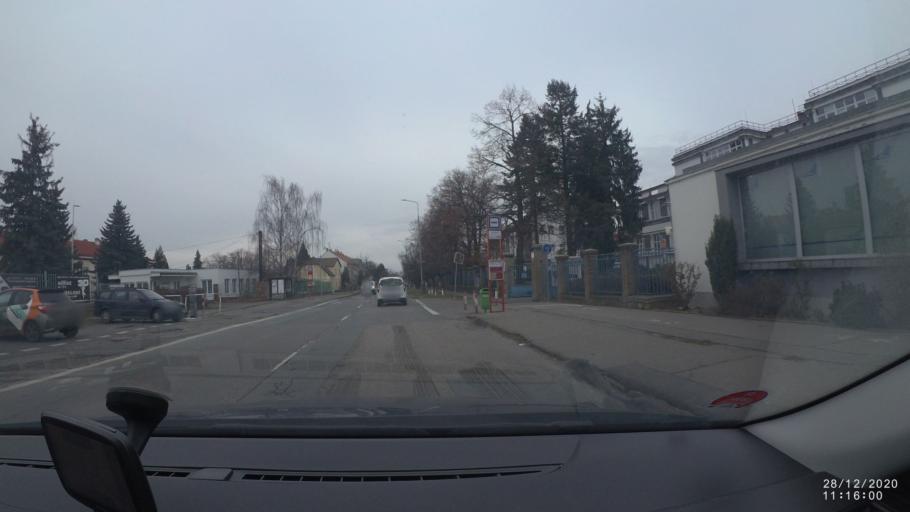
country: CZ
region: Praha
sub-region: Praha 18
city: Letnany
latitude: 50.1328
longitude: 14.5136
